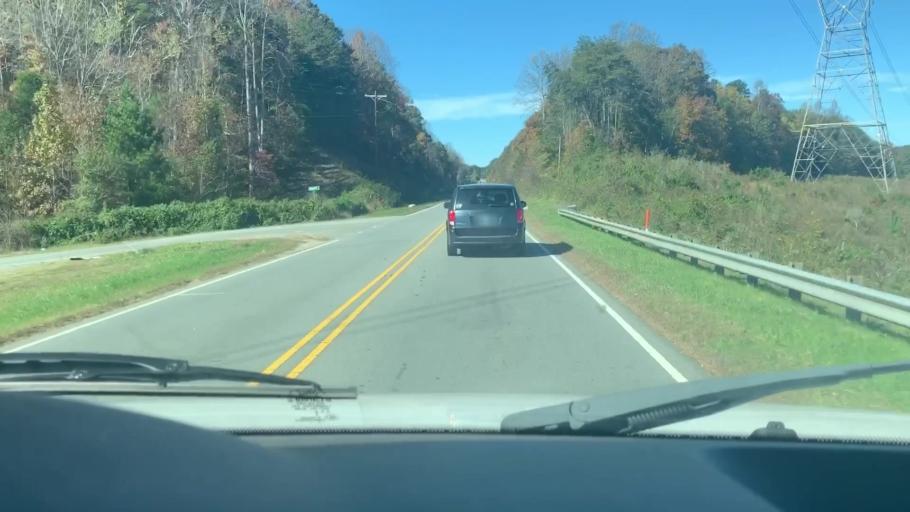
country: US
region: North Carolina
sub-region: Lincoln County
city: Lowesville
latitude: 35.4303
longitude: -80.9649
